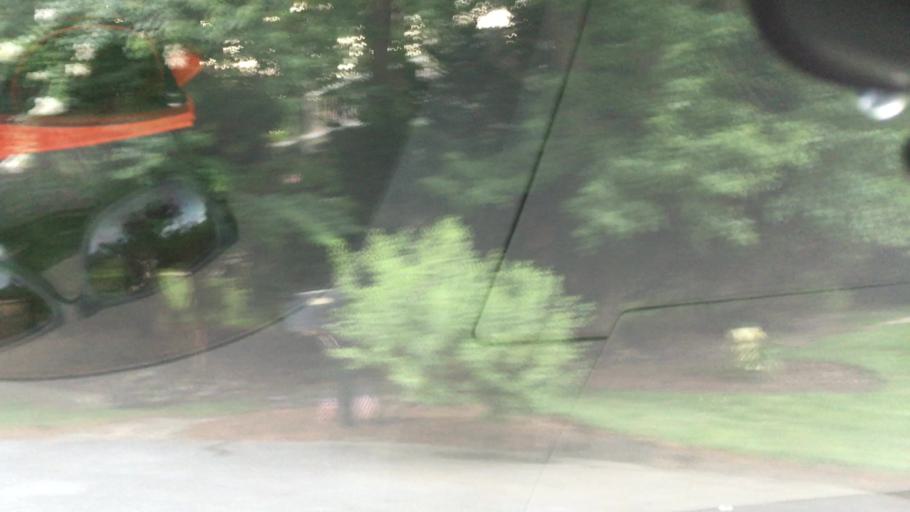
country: US
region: Delaware
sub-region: Sussex County
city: Rehoboth Beach
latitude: 38.6971
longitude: -75.0849
